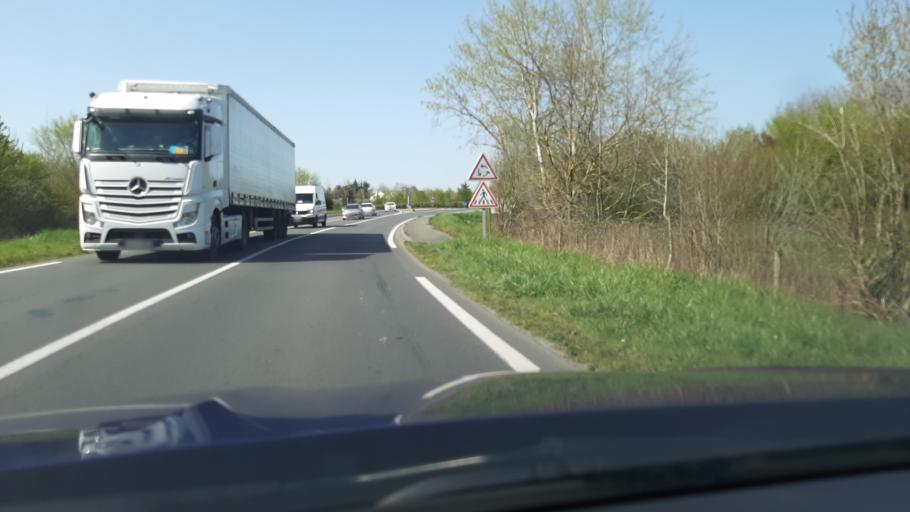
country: FR
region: Pays de la Loire
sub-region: Departement de Maine-et-Loire
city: Trelaze
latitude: 47.4820
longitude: -0.4952
